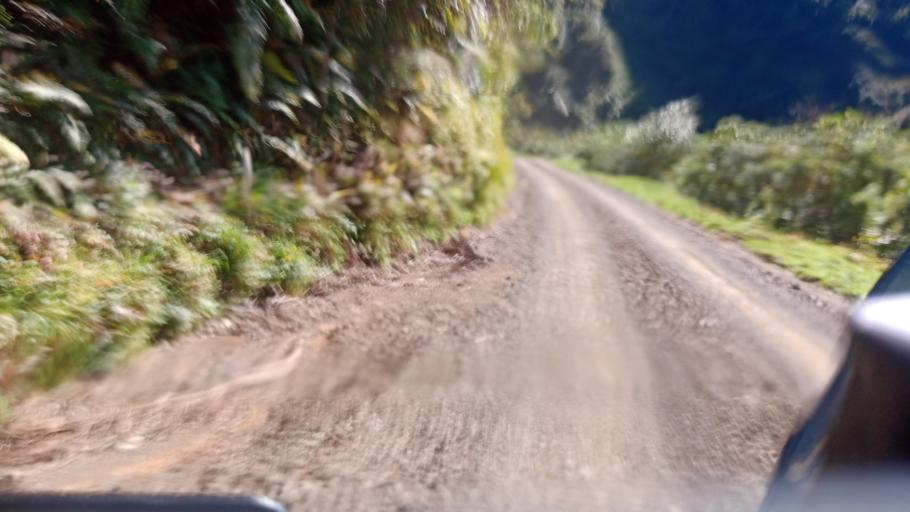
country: NZ
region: Bay of Plenty
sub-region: Opotiki District
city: Opotiki
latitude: -38.0868
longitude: 177.4778
